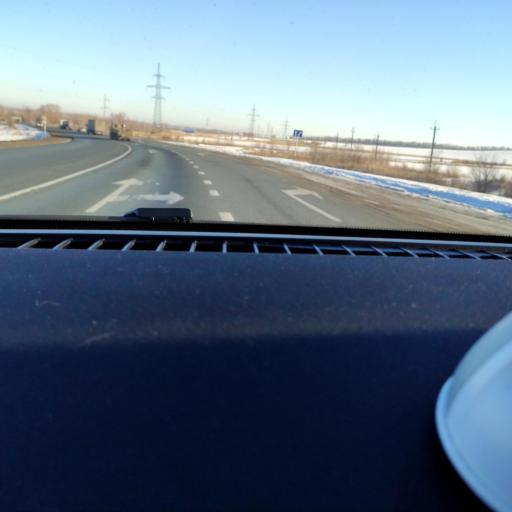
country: RU
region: Samara
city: Kinel'
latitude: 53.1485
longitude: 50.5086
